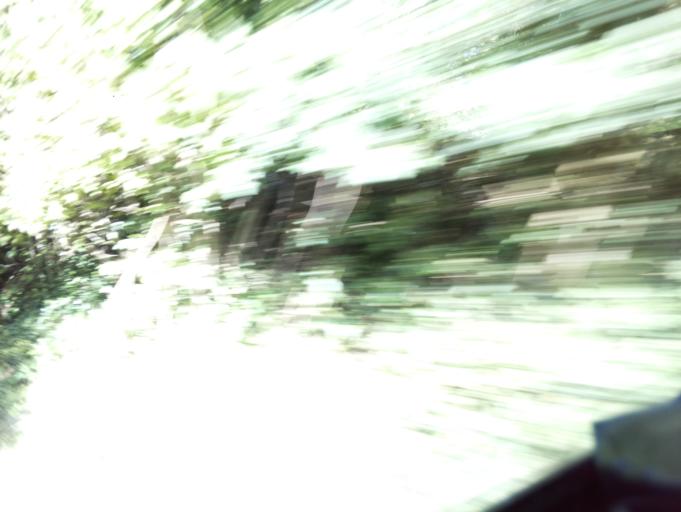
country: GB
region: England
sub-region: Hampshire
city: Winchester
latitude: 51.0822
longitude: -1.3749
